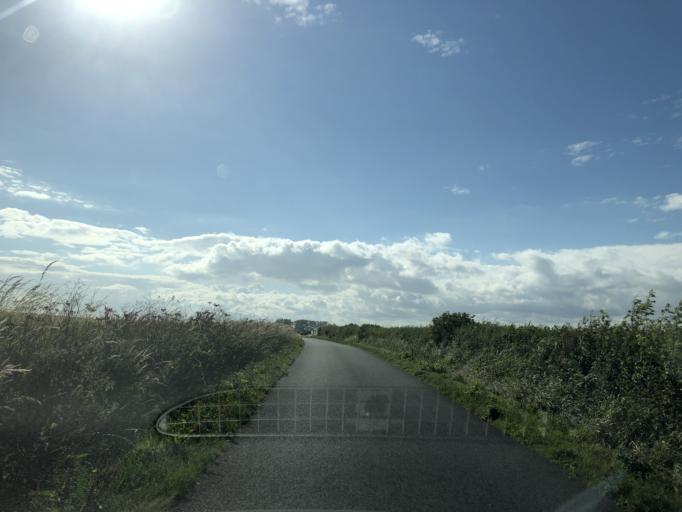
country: GB
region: England
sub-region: Isle of Wight
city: Shalfleet
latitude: 50.6887
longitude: -1.4372
